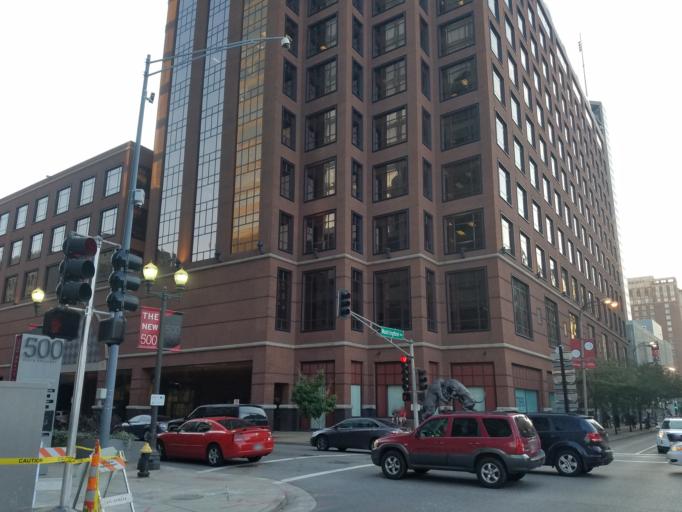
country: US
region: Missouri
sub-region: City of Saint Louis
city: St. Louis
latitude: 38.6299
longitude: -90.1881
